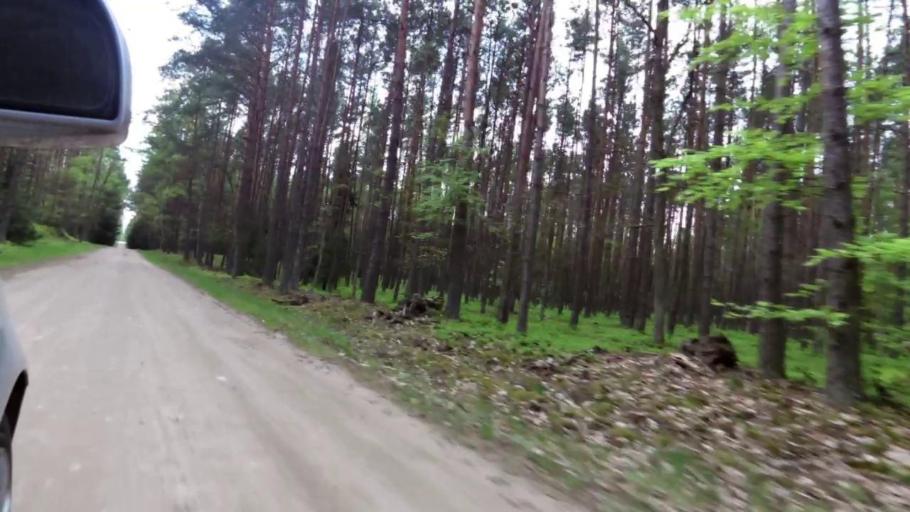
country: PL
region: West Pomeranian Voivodeship
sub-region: Powiat walecki
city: Walcz
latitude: 53.2707
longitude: 16.4017
